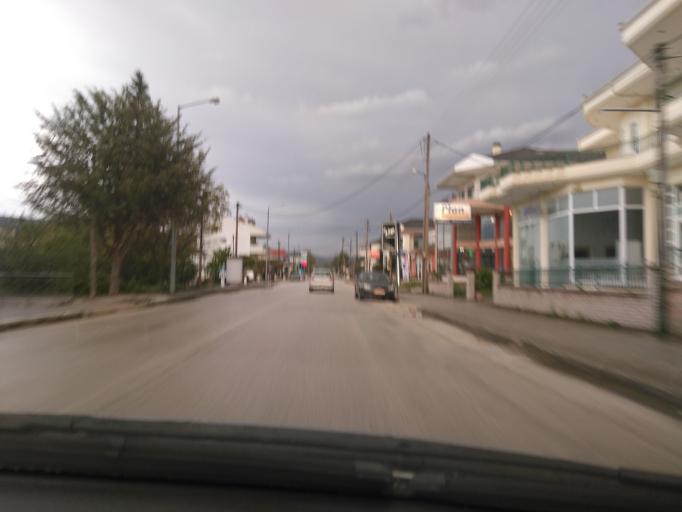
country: GR
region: Epirus
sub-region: Nomos Ioanninon
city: Katsikas
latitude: 39.6272
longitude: 20.8826
